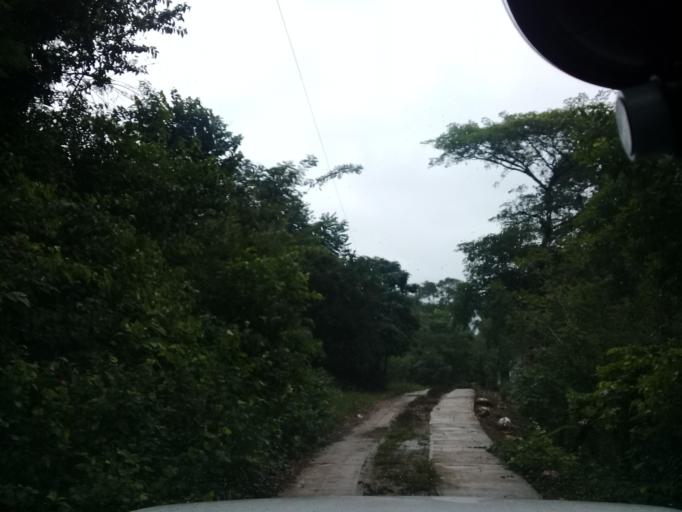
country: MX
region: Veracruz
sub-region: Chalma
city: San Pedro Coyutla
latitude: 21.2425
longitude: -98.4224
